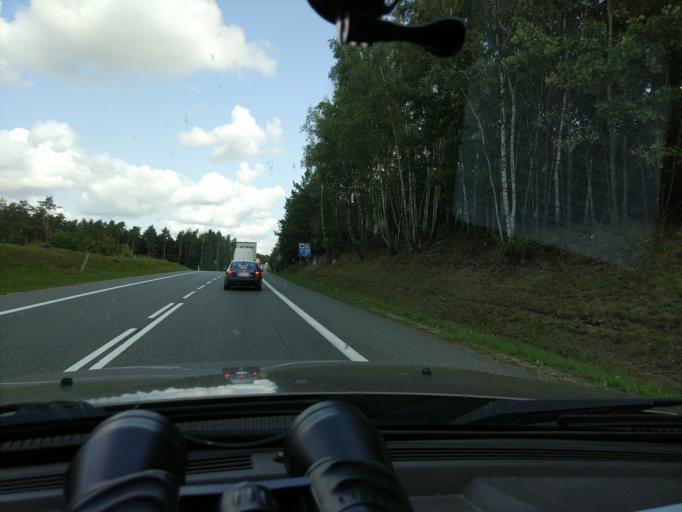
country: PL
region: Masovian Voivodeship
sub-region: Powiat mlawski
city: Mlawa
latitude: 53.1397
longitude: 20.3980
